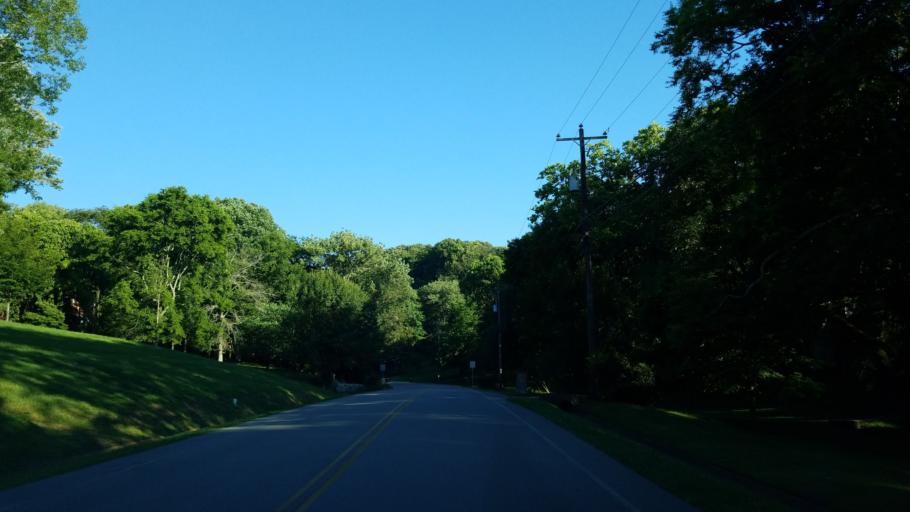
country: US
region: Tennessee
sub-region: Williamson County
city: Brentwood
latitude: 36.0480
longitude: -86.7905
